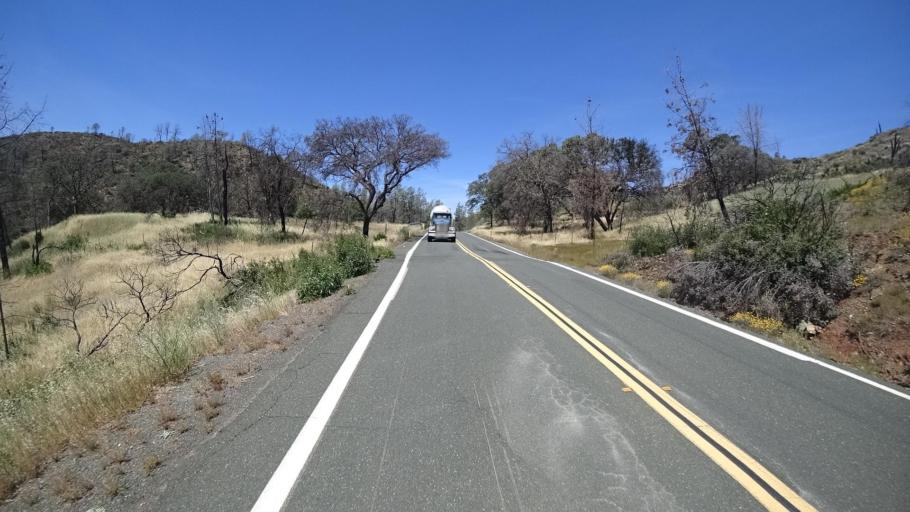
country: US
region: California
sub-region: Lake County
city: Hidden Valley Lake
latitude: 38.7148
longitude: -122.4856
